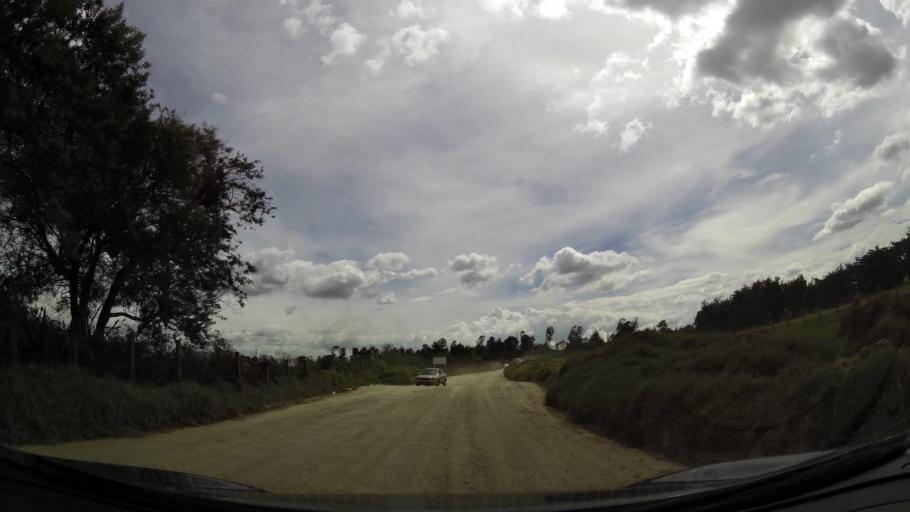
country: CO
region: Cundinamarca
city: Funza
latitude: 4.7146
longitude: -74.1731
